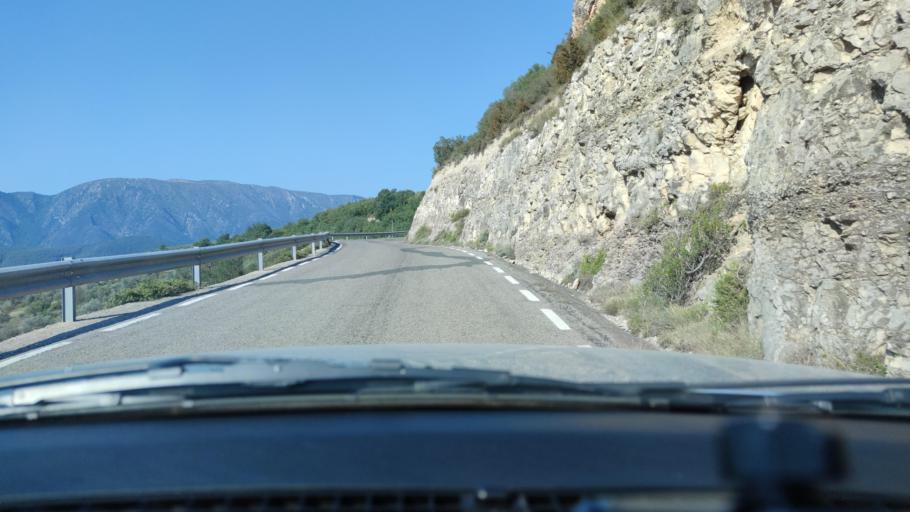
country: ES
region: Catalonia
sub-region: Provincia de Lleida
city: Llimiana
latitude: 42.0878
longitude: 0.8721
